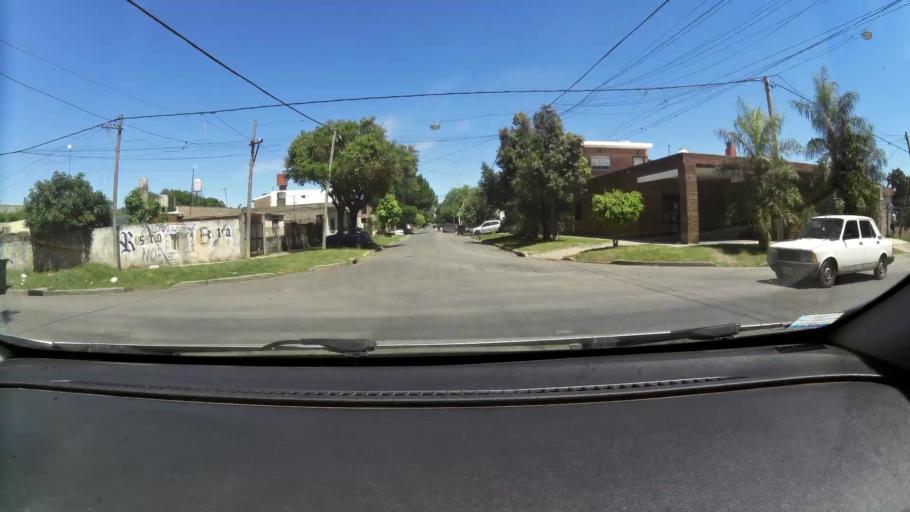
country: AR
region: Santa Fe
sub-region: Departamento de Rosario
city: Rosario
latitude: -32.9521
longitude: -60.7086
